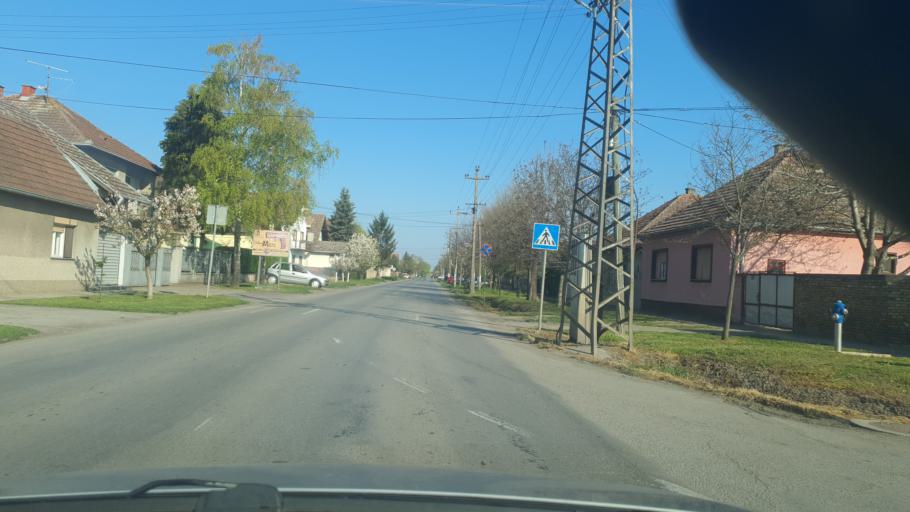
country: RS
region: Autonomna Pokrajina Vojvodina
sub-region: Juznobacki Okrug
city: Vrbas
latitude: 45.5575
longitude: 19.6631
